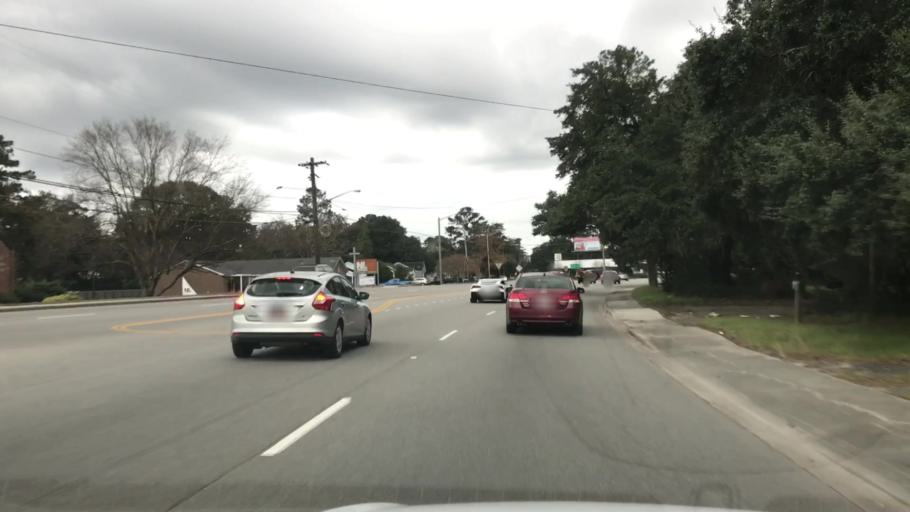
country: US
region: South Carolina
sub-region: Georgetown County
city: Georgetown
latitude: 33.3504
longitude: -79.2930
